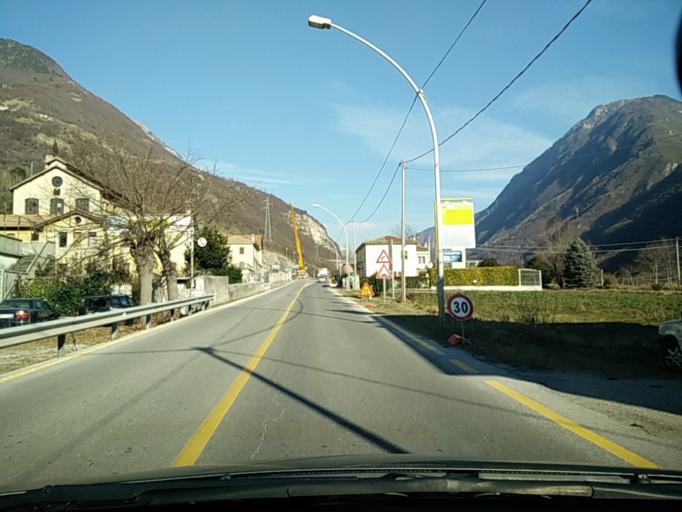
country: IT
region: Veneto
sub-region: Provincia di Treviso
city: Revine
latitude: 46.0189
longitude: 12.2905
